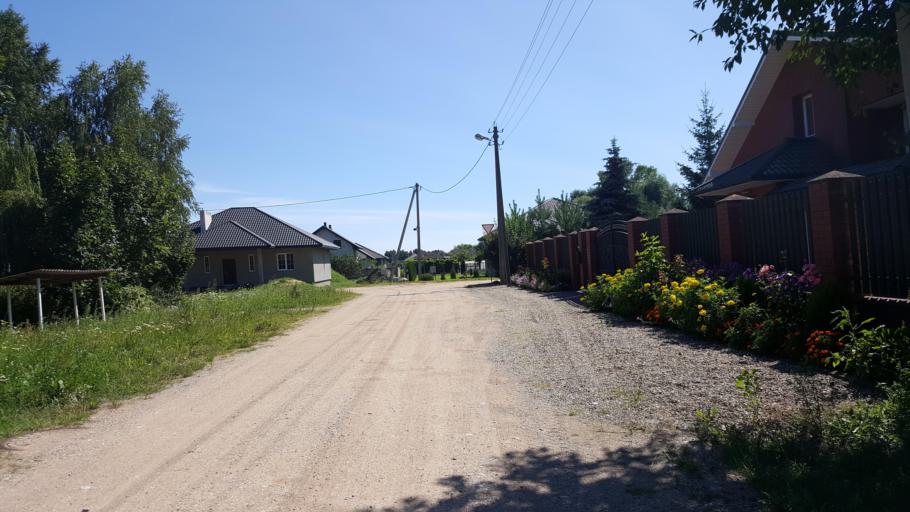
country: BY
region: Brest
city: Charnawchytsy
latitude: 52.2101
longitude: 23.7513
